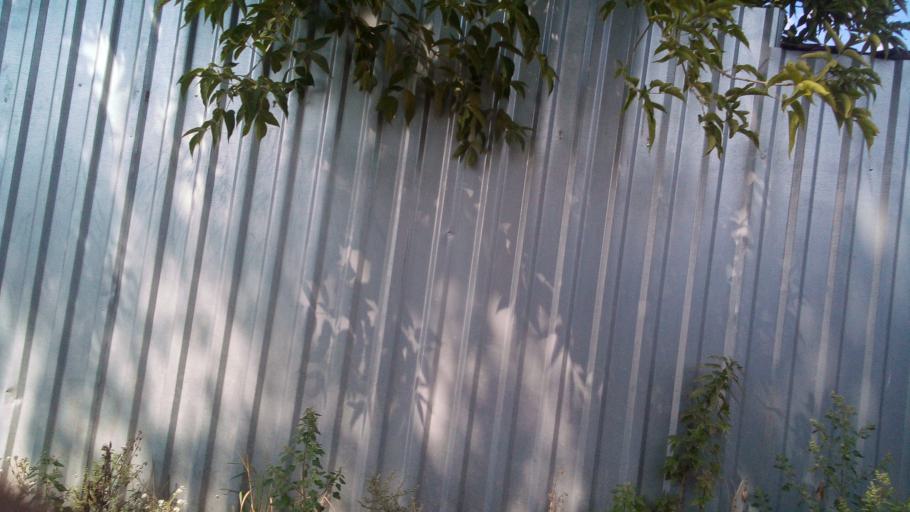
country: RU
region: Chelyabinsk
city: Ozersk
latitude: 55.7880
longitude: 60.7467
